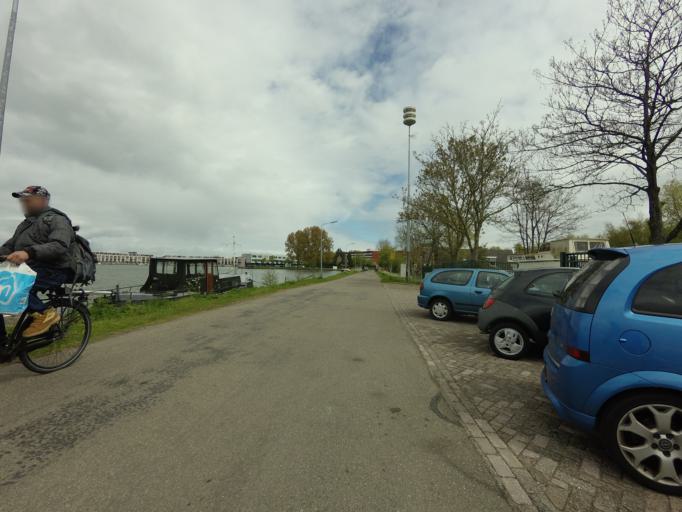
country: NL
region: North Holland
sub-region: Gemeente Amsterdam
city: Driemond
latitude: 52.3064
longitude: 5.0250
